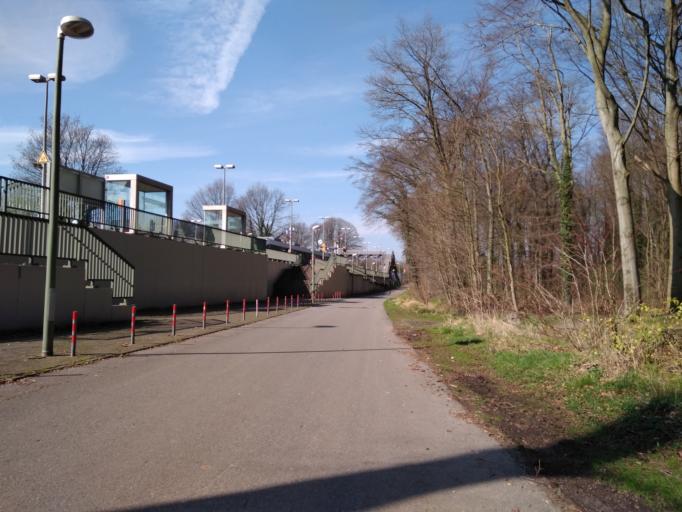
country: DE
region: North Rhine-Westphalia
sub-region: Regierungsbezirk Munster
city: Gladbeck
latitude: 51.6146
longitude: 6.9739
